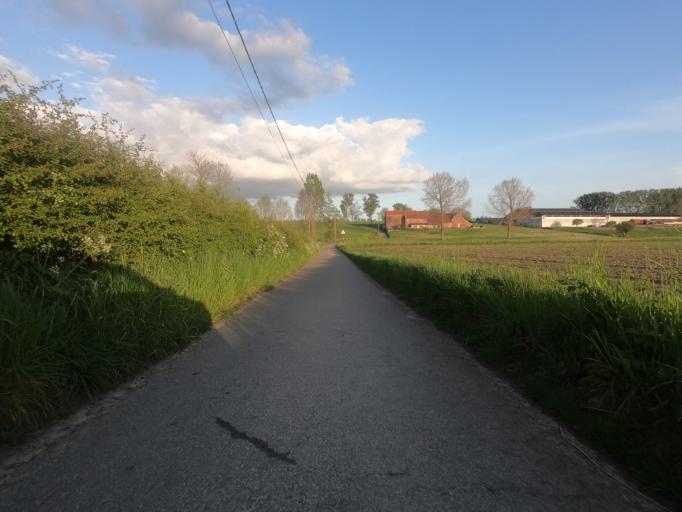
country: BE
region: Flanders
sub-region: Provincie Vlaams-Brabant
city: Pepingen
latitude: 50.7739
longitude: 4.1423
